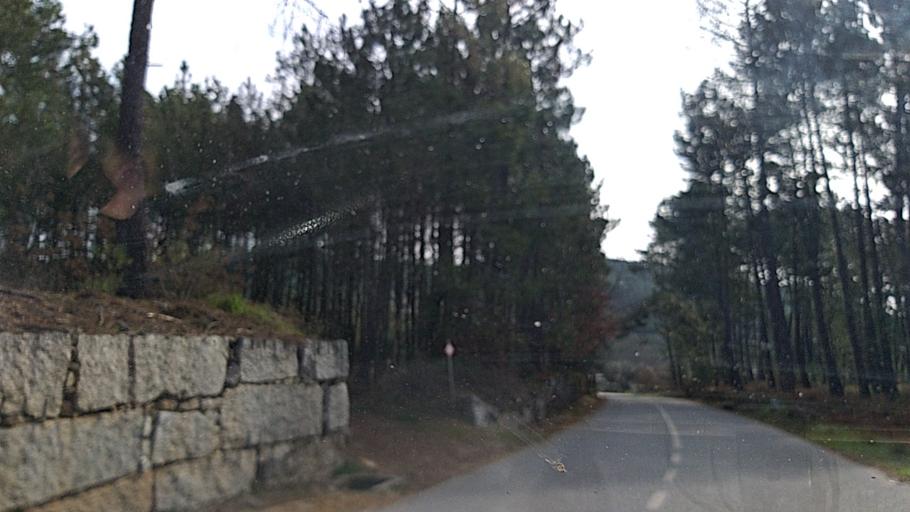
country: PT
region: Guarda
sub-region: Fornos de Algodres
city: Fornos de Algodres
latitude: 40.6889
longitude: -7.5449
